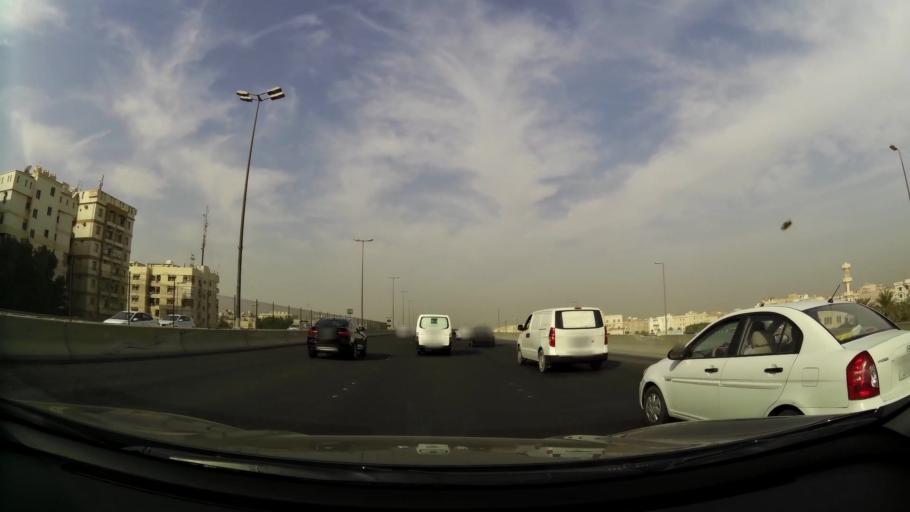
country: KW
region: Al Farwaniyah
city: Al Farwaniyah
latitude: 29.2669
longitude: 47.9417
